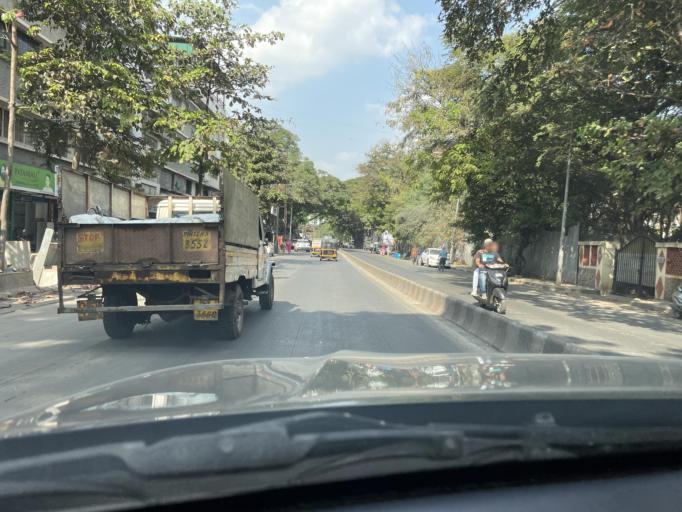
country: IN
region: Maharashtra
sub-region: Pune Division
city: Pune
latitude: 18.4997
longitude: 73.9004
